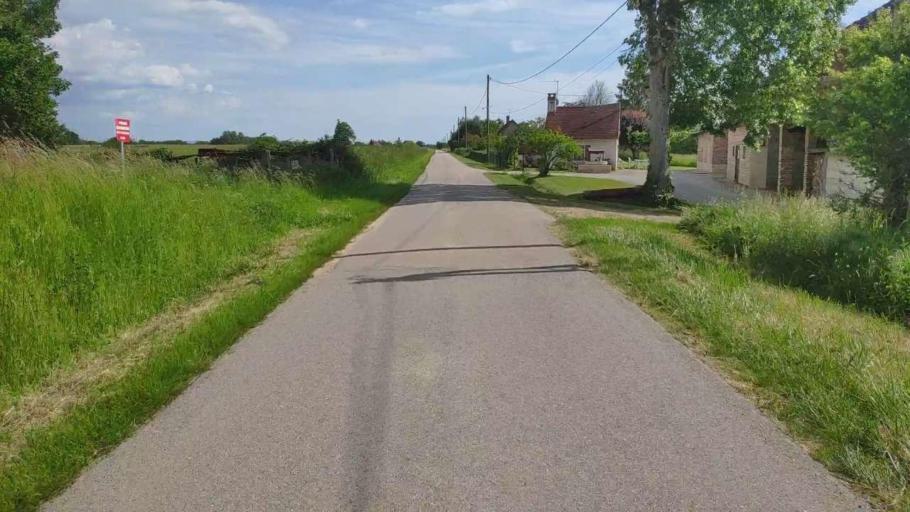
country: FR
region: Franche-Comte
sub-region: Departement du Jura
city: Bletterans
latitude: 46.8183
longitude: 5.3796
